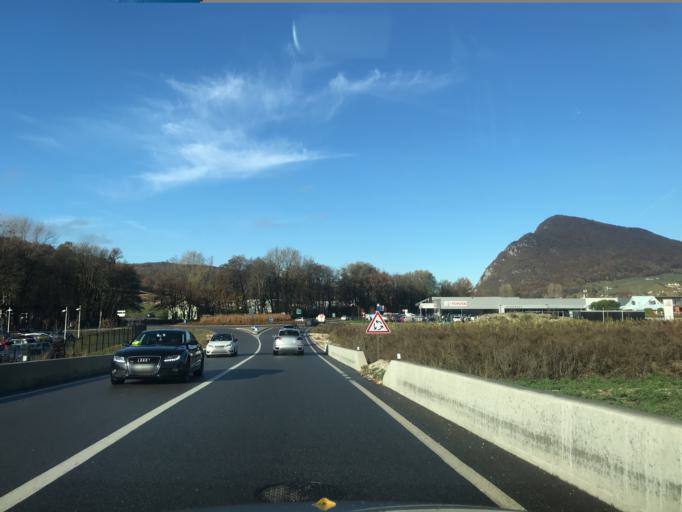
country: FR
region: Rhone-Alpes
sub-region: Departement de la Haute-Savoie
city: Epagny
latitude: 45.9312
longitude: 6.0835
